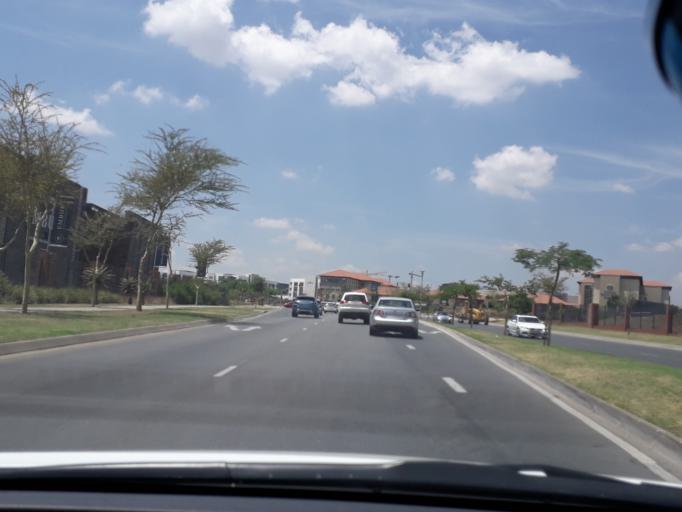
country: ZA
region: Gauteng
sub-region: City of Johannesburg Metropolitan Municipality
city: Midrand
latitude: -26.0139
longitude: 28.0974
